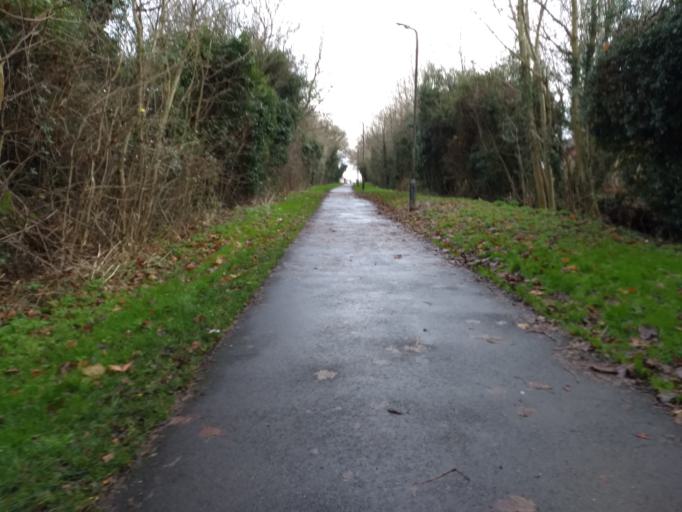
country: GB
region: England
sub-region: Buckinghamshire
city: Newton Longville
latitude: 51.9956
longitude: -0.7675
